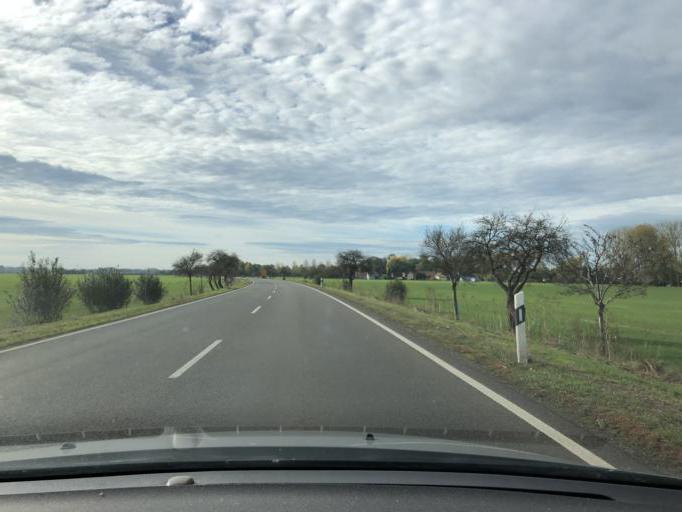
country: DE
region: Saxony
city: Pegau
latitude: 51.1570
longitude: 12.2499
